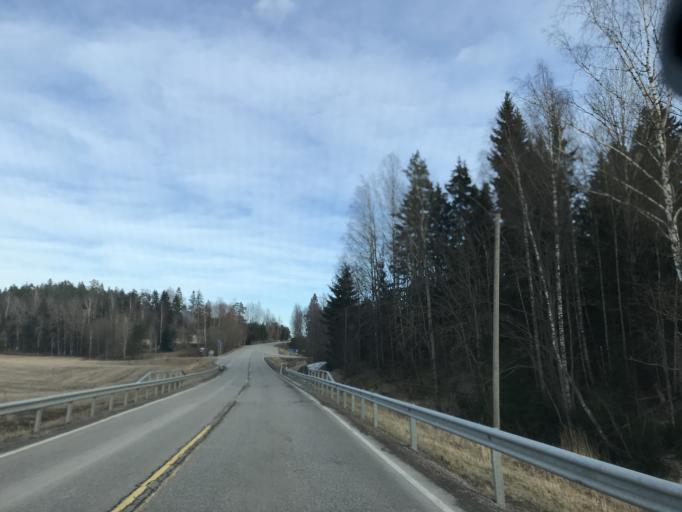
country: FI
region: Uusimaa
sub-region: Raaseporin
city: Pohja
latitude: 60.0920
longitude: 23.4784
